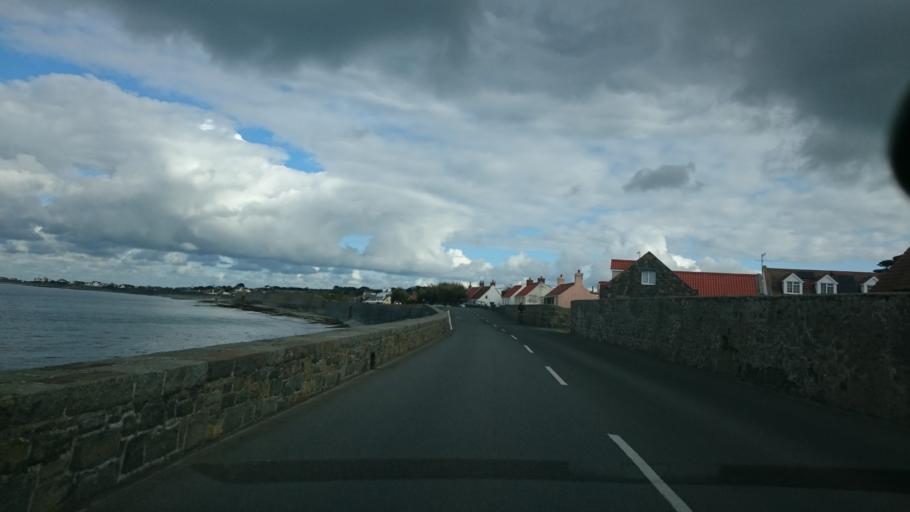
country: GG
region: St Peter Port
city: Saint Peter Port
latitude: 49.4404
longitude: -2.6516
